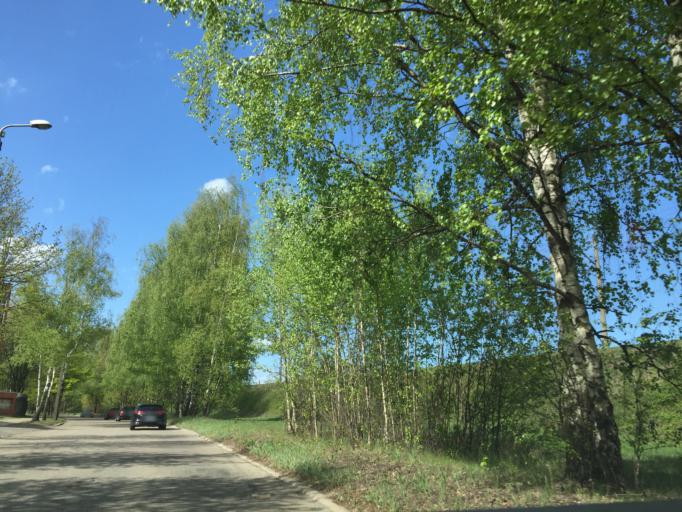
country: LV
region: Riga
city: Jaunciems
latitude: 57.0294
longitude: 24.1371
